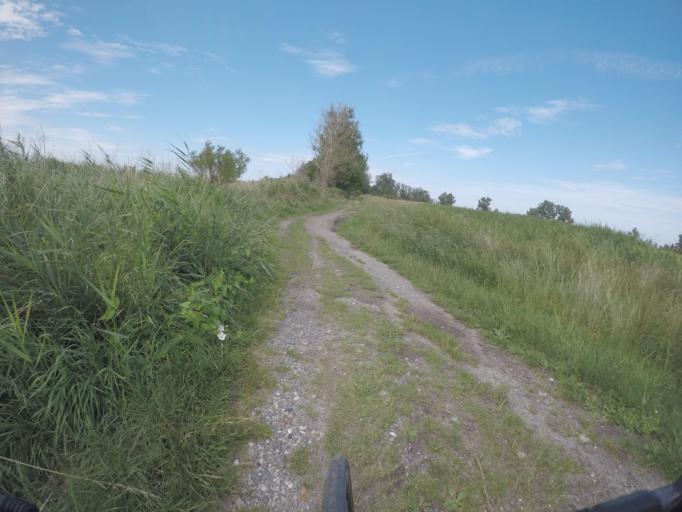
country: DE
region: Mecklenburg-Vorpommern
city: Altefahr
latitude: 54.3632
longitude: 13.1237
